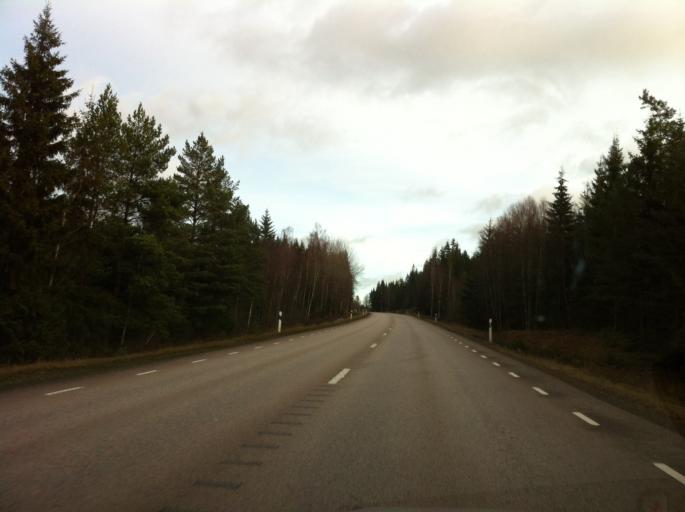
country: SE
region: Kronoberg
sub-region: Uppvidinge Kommun
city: Aseda
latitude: 57.1481
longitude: 15.3004
